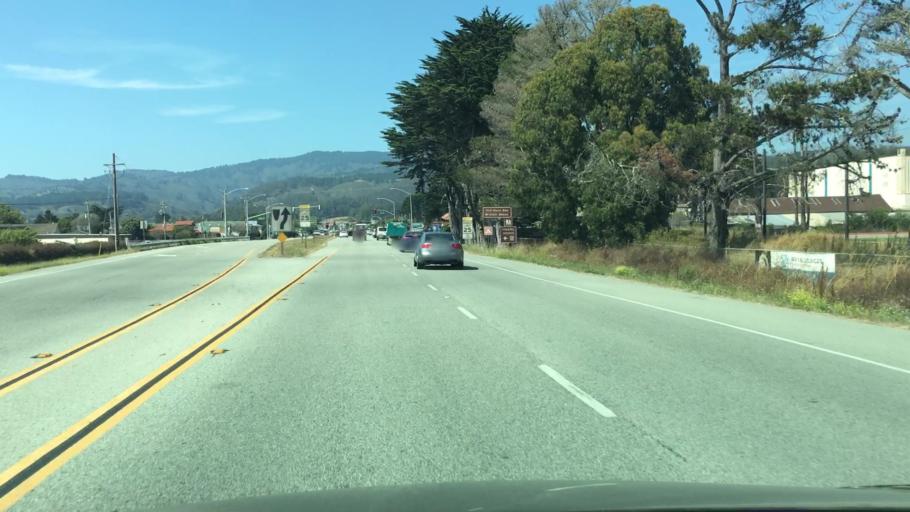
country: US
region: California
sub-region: San Mateo County
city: Half Moon Bay
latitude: 37.4627
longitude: -122.4351
